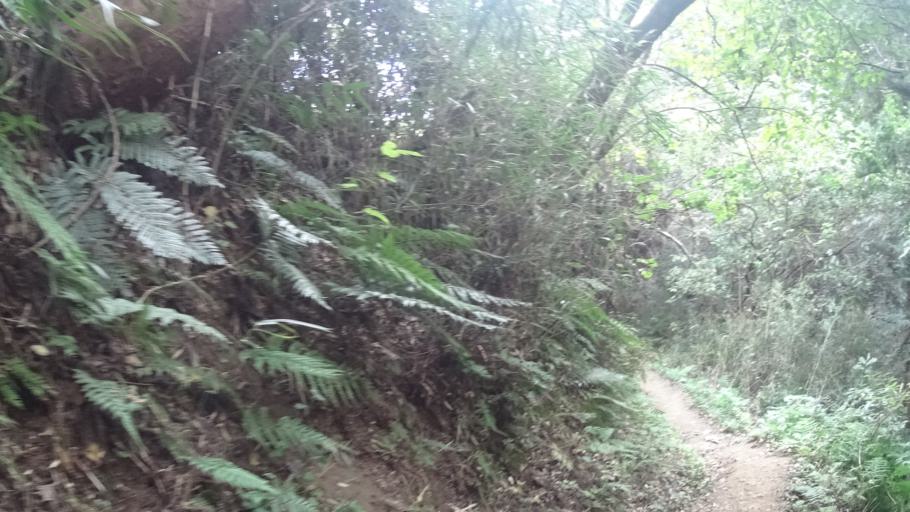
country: JP
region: Kanagawa
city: Zushi
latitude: 35.2845
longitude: 139.6092
